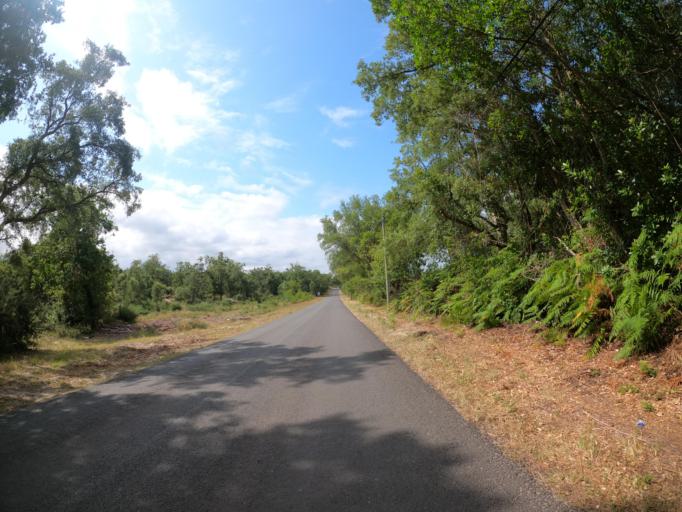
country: FR
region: Aquitaine
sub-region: Departement des Landes
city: Leon
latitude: 43.8926
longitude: -1.3671
